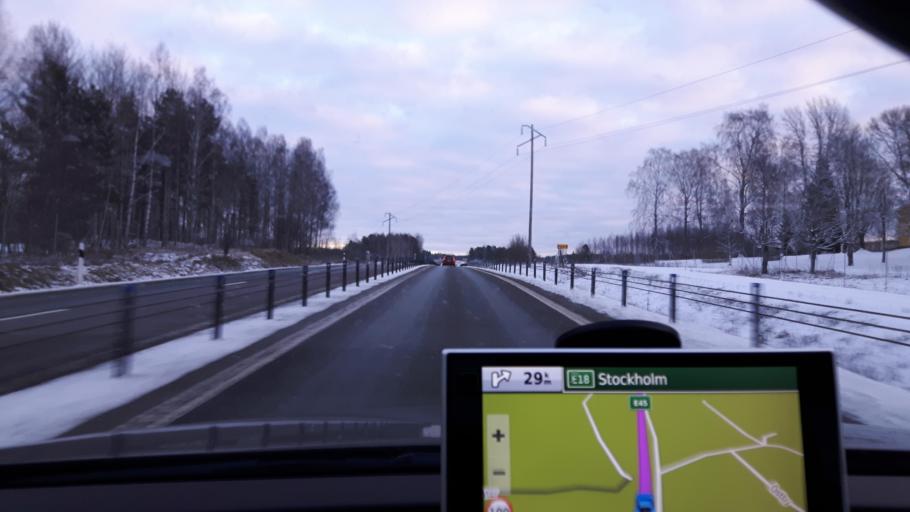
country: SE
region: Vaestra Goetaland
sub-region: Amals Kommun
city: Amal
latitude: 59.0905
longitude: 12.7235
